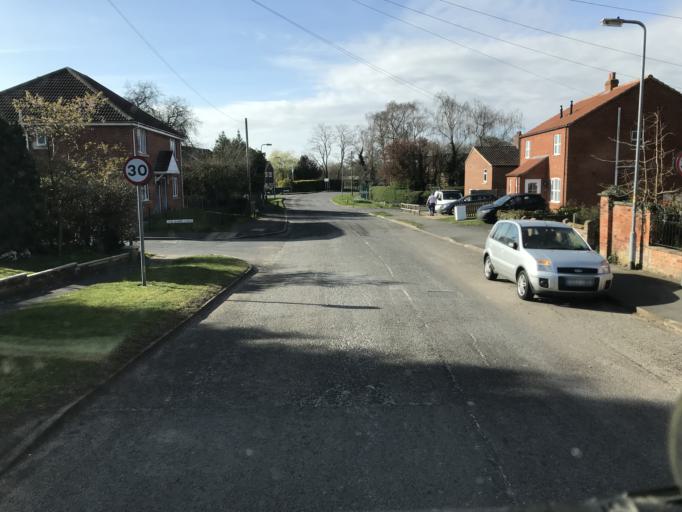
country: GB
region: England
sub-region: Lincolnshire
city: Market Rasen
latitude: 53.3900
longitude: -0.3311
